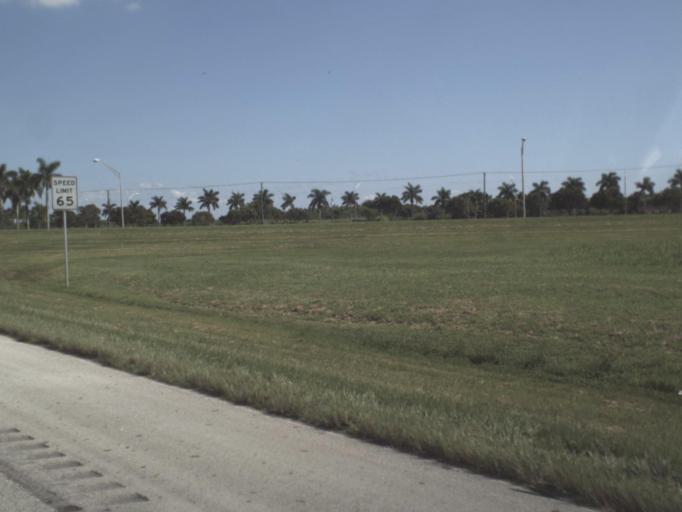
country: US
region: Florida
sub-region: Miami-Dade County
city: Naranja
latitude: 25.5079
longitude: -80.4152
